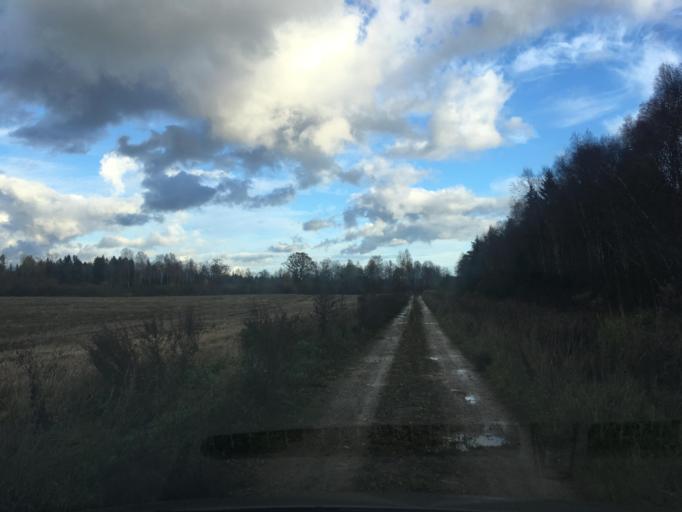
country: EE
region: Harju
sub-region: Raasiku vald
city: Arukula
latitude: 59.3578
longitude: 25.1044
